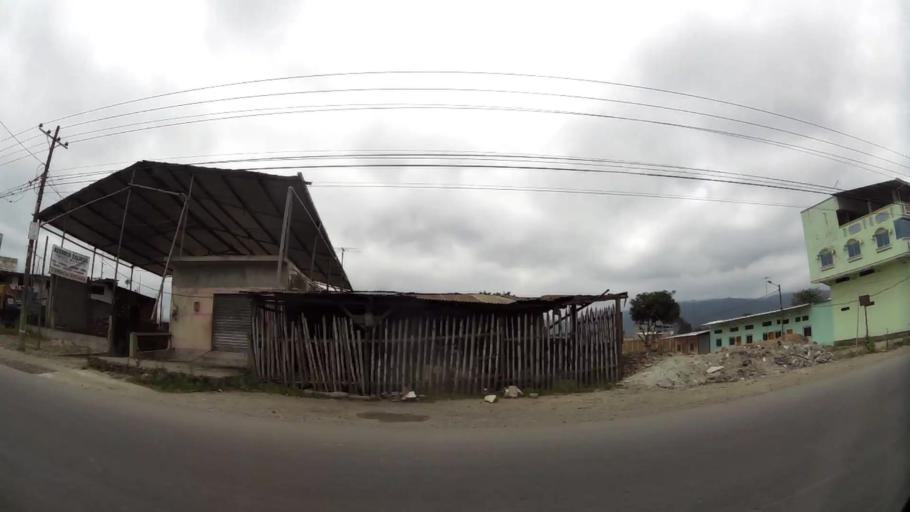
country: EC
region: Guayas
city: Naranjal
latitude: -2.6813
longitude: -79.6206
